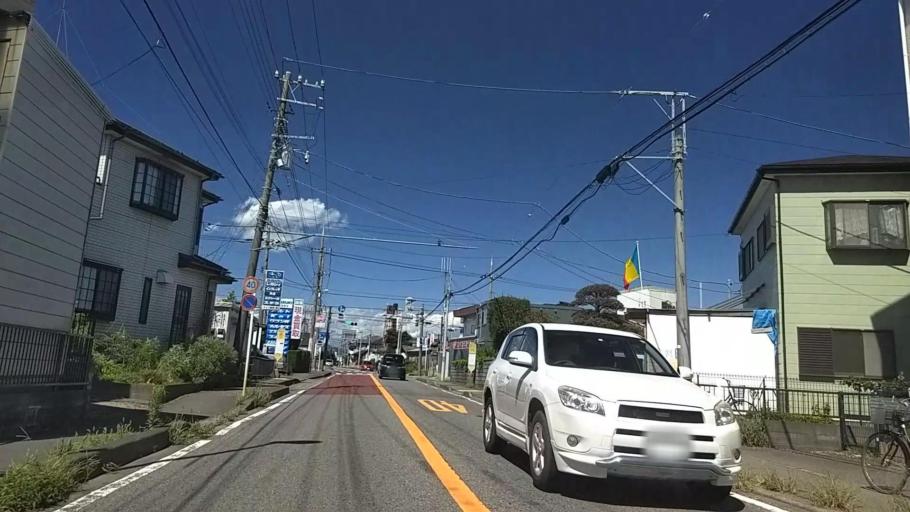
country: JP
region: Kanagawa
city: Zama
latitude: 35.5518
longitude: 139.3339
